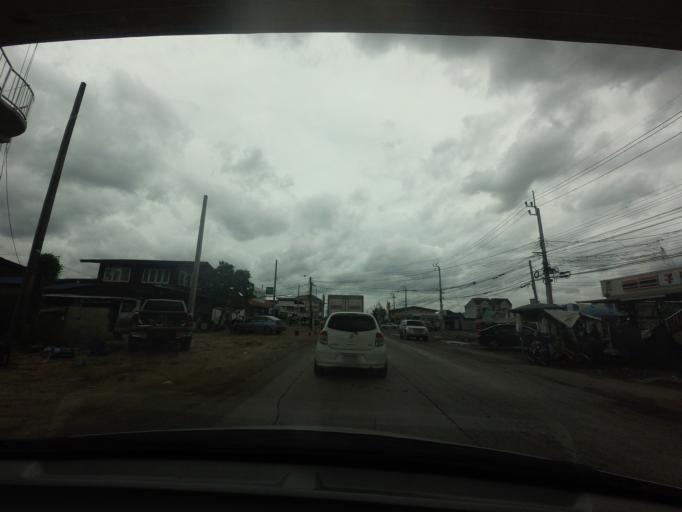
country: TH
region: Bangkok
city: Lat Krabang
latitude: 13.7654
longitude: 100.7761
